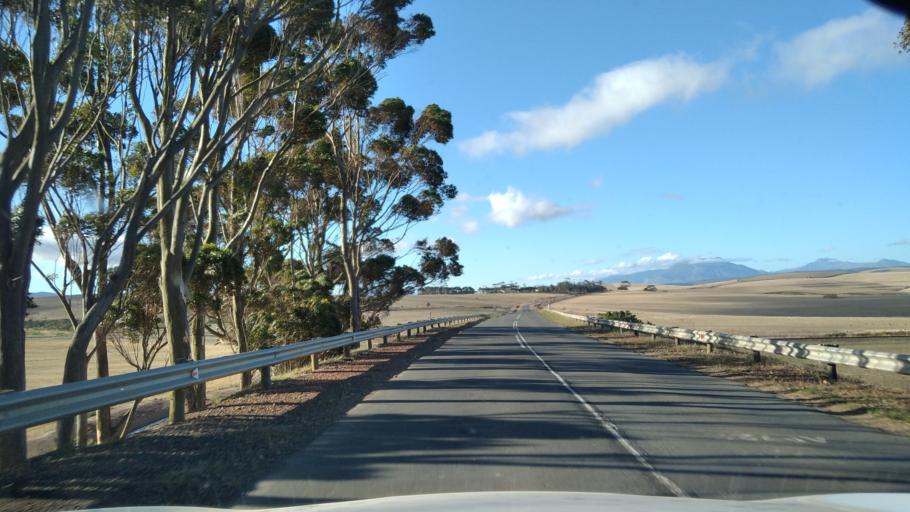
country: ZA
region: Western Cape
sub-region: Overberg District Municipality
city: Caledon
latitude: -34.2125
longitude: 19.2731
